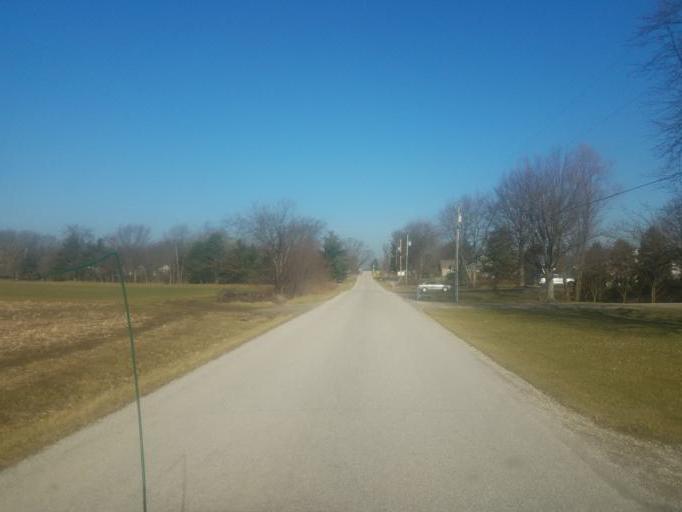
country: US
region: Ohio
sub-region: Seneca County
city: Tiffin
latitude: 41.1130
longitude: -83.1119
